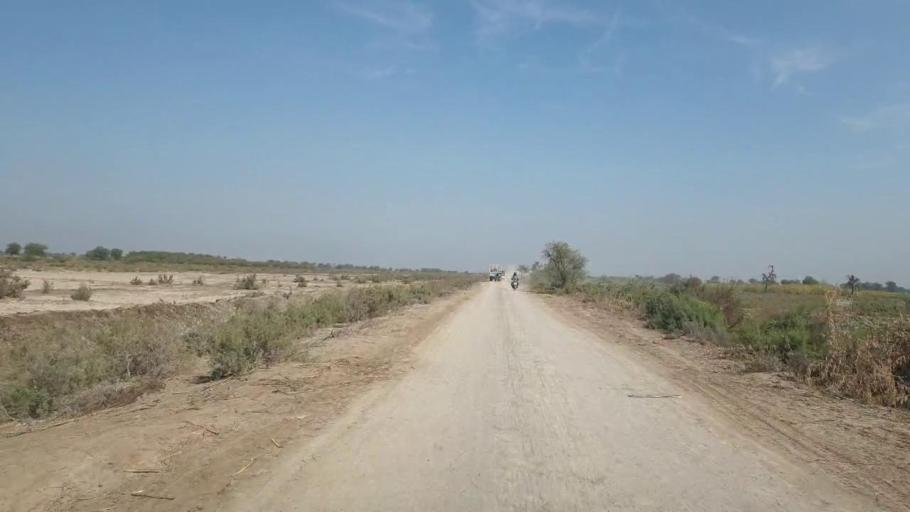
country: PK
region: Sindh
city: Samaro
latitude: 25.3256
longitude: 69.2418
